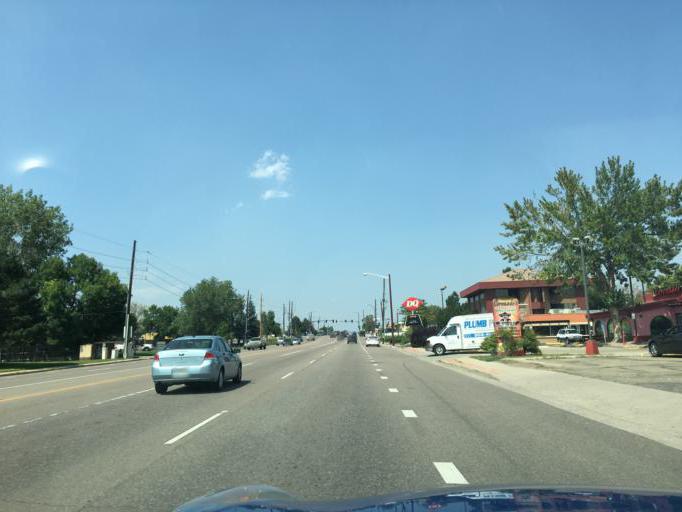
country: US
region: Colorado
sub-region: Adams County
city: Westminster
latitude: 39.8393
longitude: -105.0532
